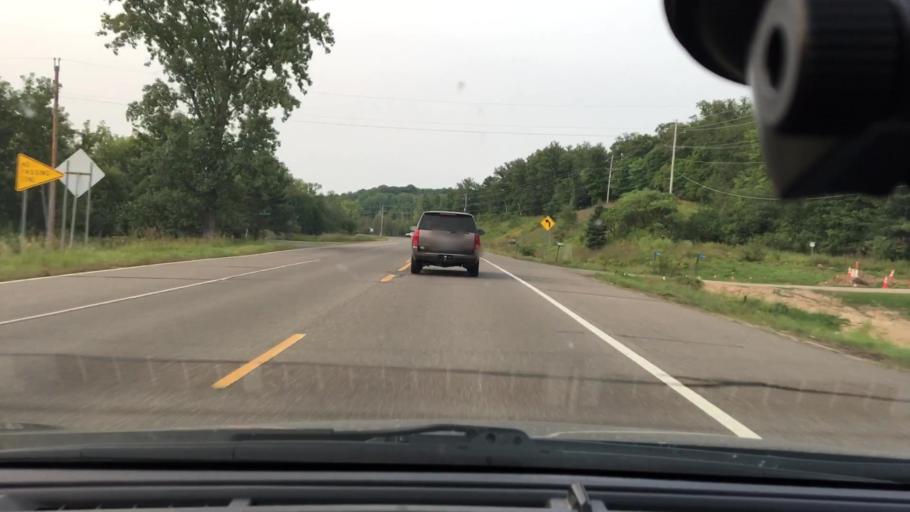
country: US
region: Minnesota
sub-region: Crow Wing County
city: Crosby
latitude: 46.4815
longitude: -93.8986
